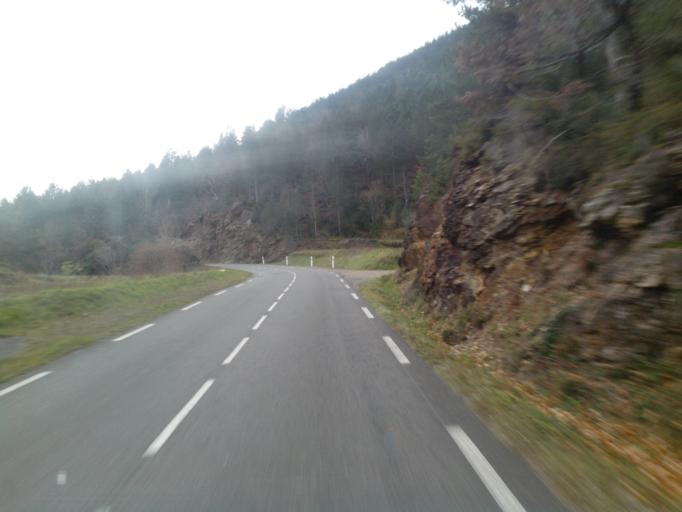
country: FR
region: Languedoc-Roussillon
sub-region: Departement de la Lozere
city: Florac
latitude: 44.3042
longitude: 3.5964
